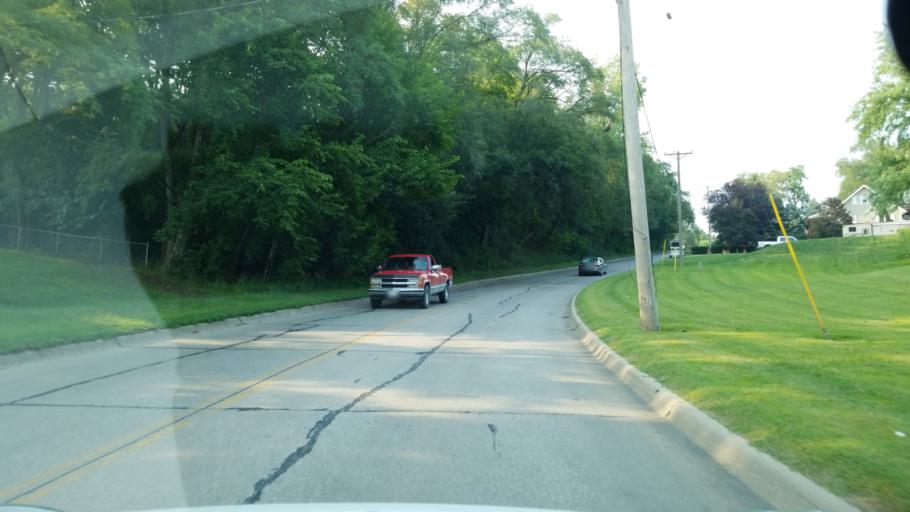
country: US
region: Nebraska
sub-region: Sarpy County
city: Bellevue
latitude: 41.1285
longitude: -95.8923
